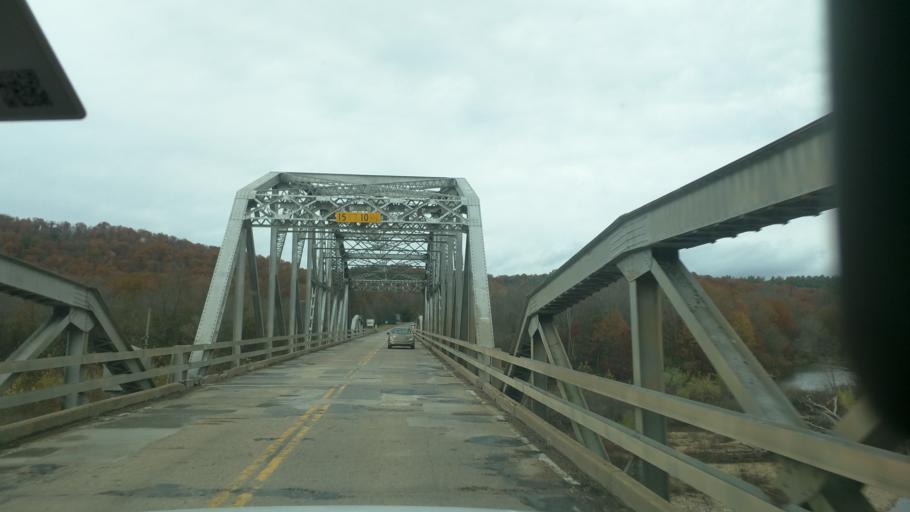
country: US
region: Oklahoma
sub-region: Cherokee County
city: Tahlequah
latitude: 35.9214
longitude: -94.8373
